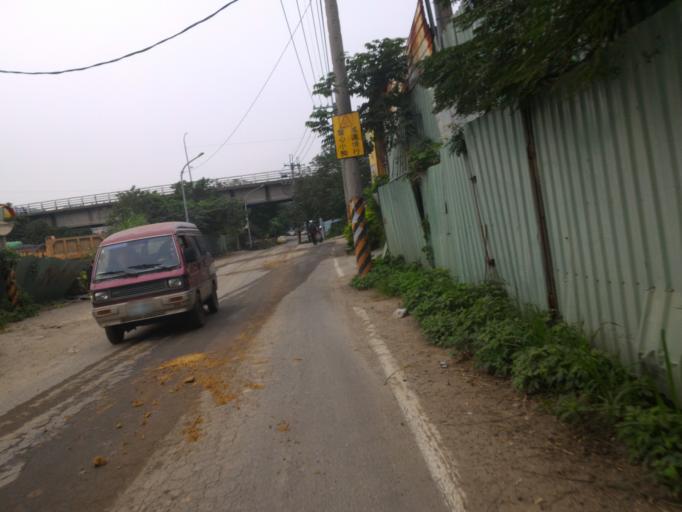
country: TW
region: Taipei
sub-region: Taipei
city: Banqiao
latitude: 24.9608
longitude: 121.4091
